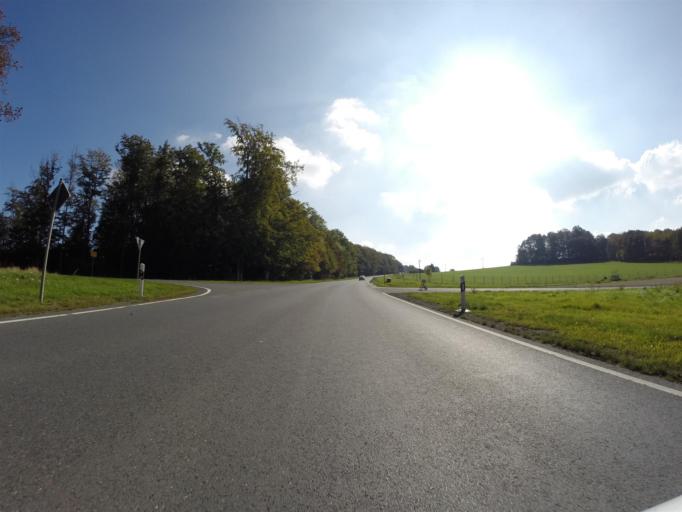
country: DE
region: Thuringia
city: Schleiz
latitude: 50.5586
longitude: 11.8107
